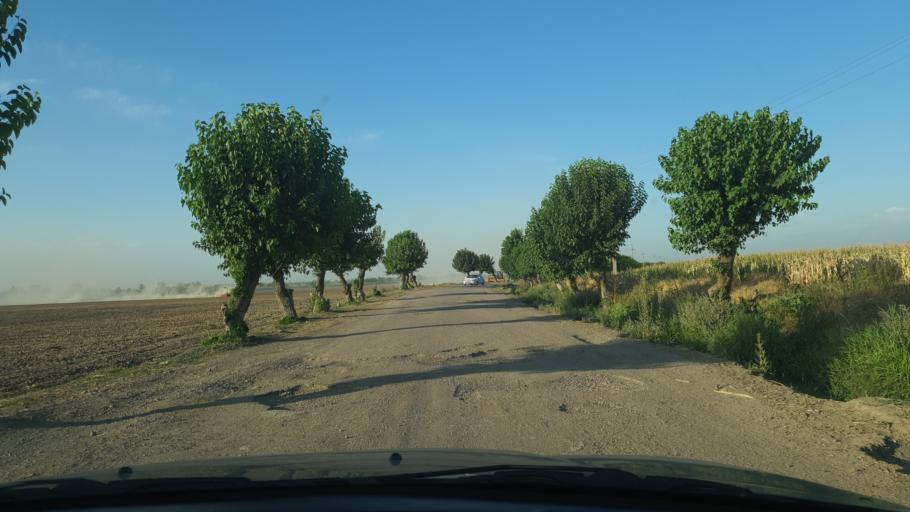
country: UZ
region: Toshkent
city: Tuytepa
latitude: 41.0963
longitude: 69.3739
